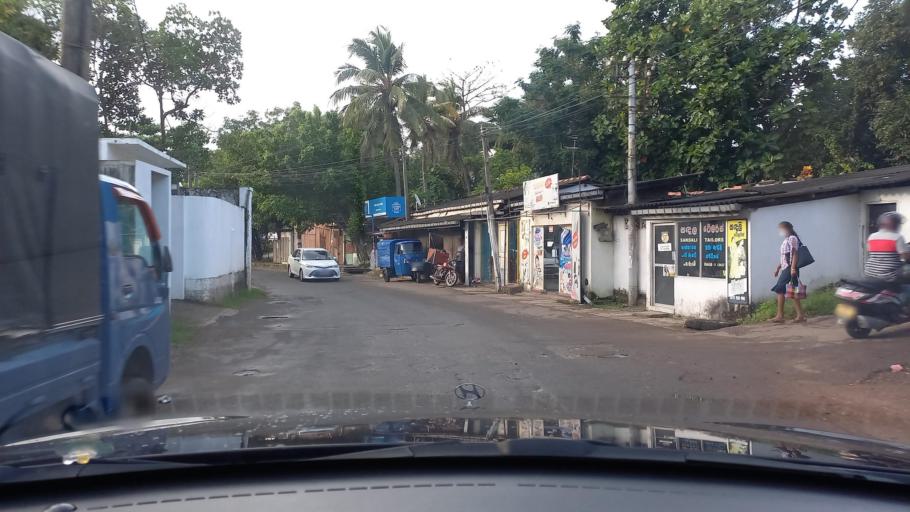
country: LK
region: Western
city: Pita Kotte
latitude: 6.8746
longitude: 79.8854
